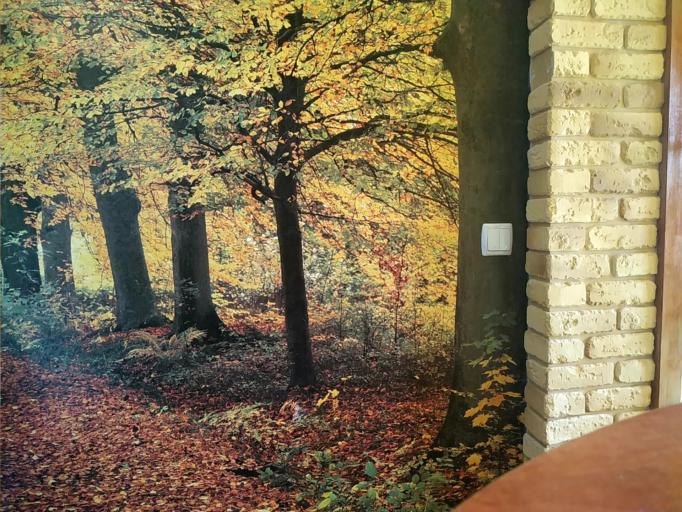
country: RU
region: Jaroslavl
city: Kukoboy
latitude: 58.9006
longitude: 39.6936
